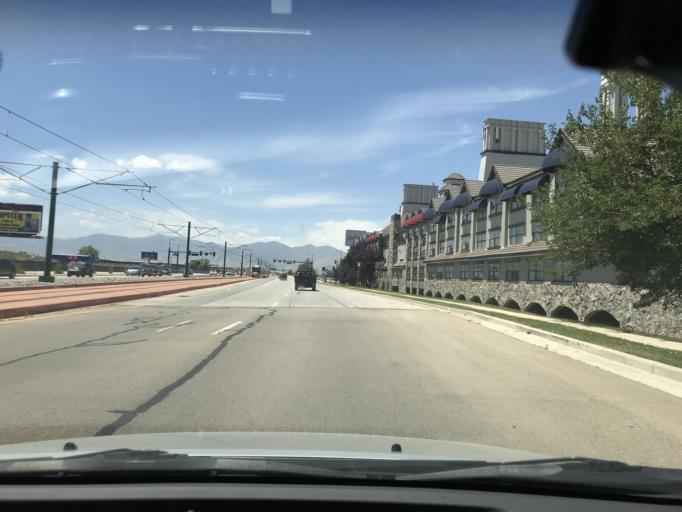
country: US
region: Utah
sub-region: Salt Lake County
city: Salt Lake City
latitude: 40.7712
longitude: -111.9513
